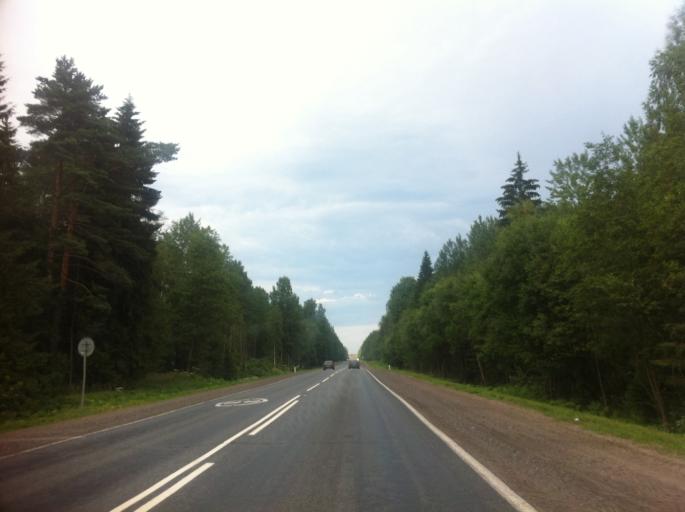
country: RU
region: Pskov
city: Strugi-Krasnyye
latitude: 58.1382
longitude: 29.1721
